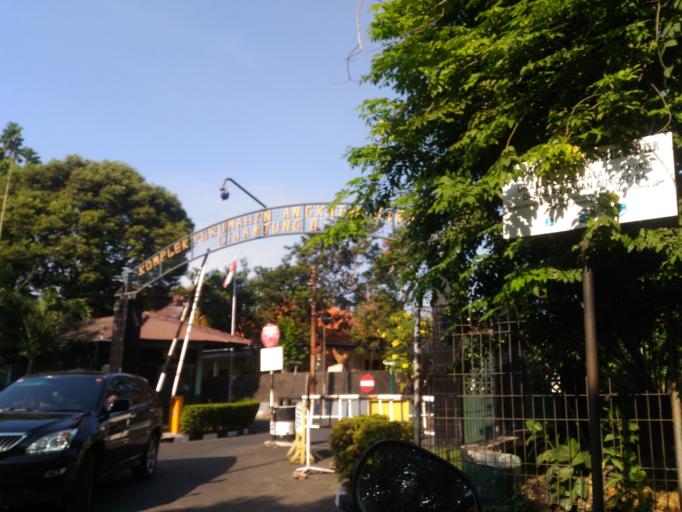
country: ID
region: Jakarta Raya
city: Jakarta
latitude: -6.3096
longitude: 106.8593
